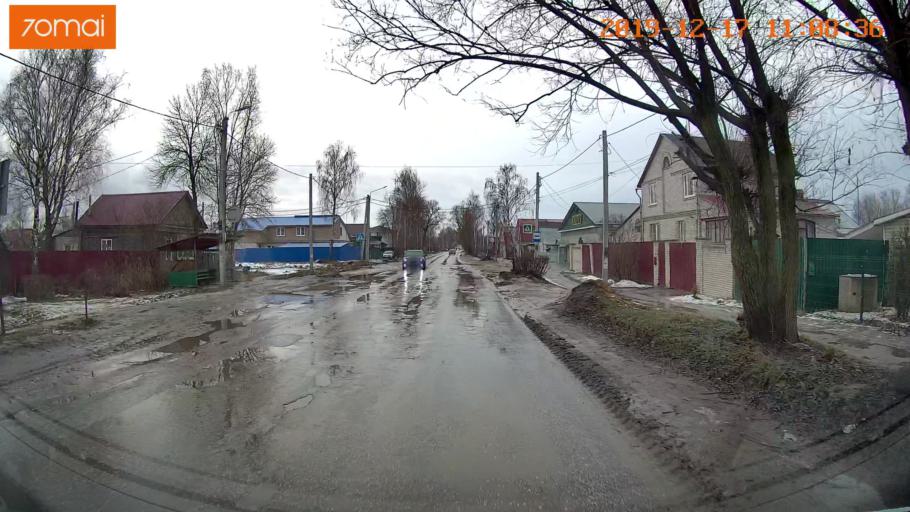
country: RU
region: Vladimir
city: Gus'-Khrustal'nyy
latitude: 55.6067
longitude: 40.6432
